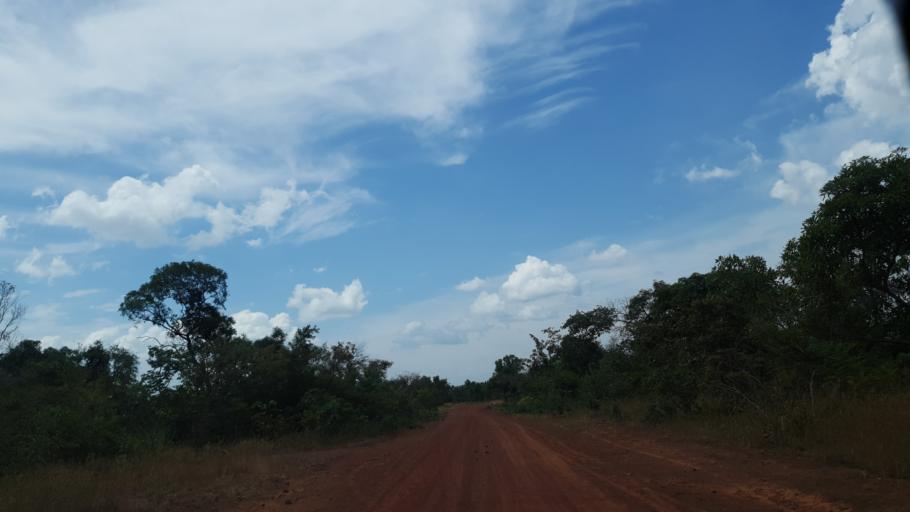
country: ML
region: Sikasso
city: Sikasso
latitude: 11.6855
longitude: -6.2072
